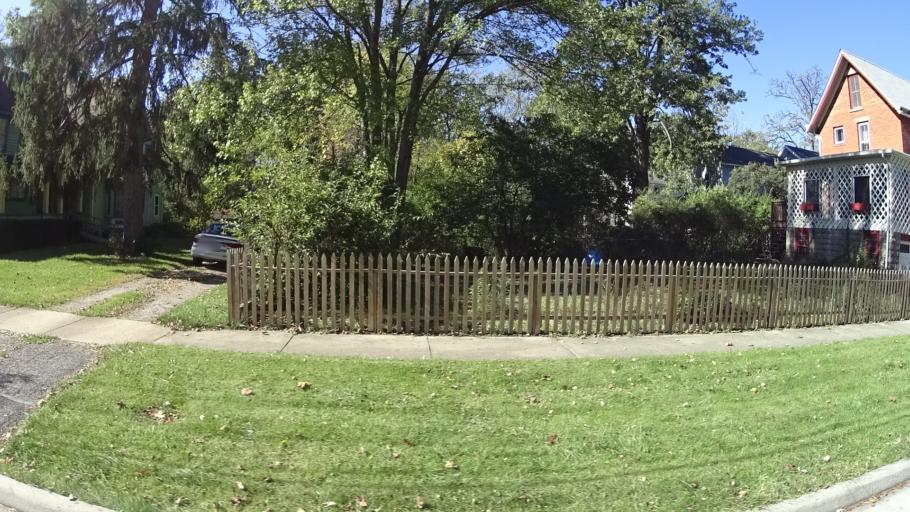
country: US
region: Ohio
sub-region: Lorain County
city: Oberlin
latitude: 41.2913
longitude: -82.2248
